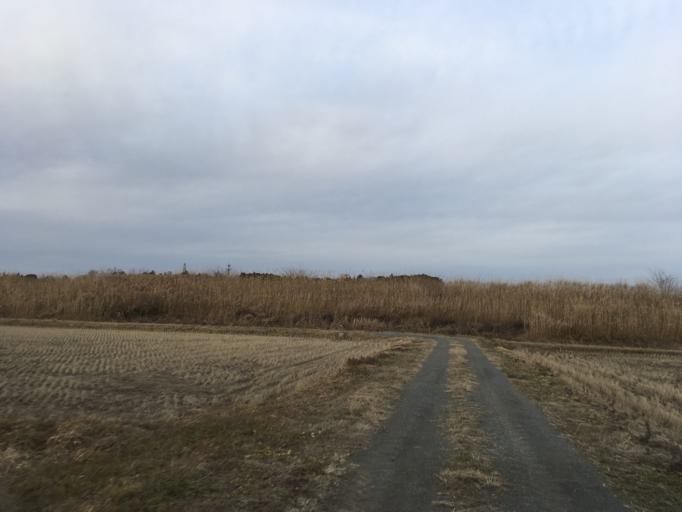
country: JP
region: Miyagi
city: Kogota
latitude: 38.6458
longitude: 141.0697
